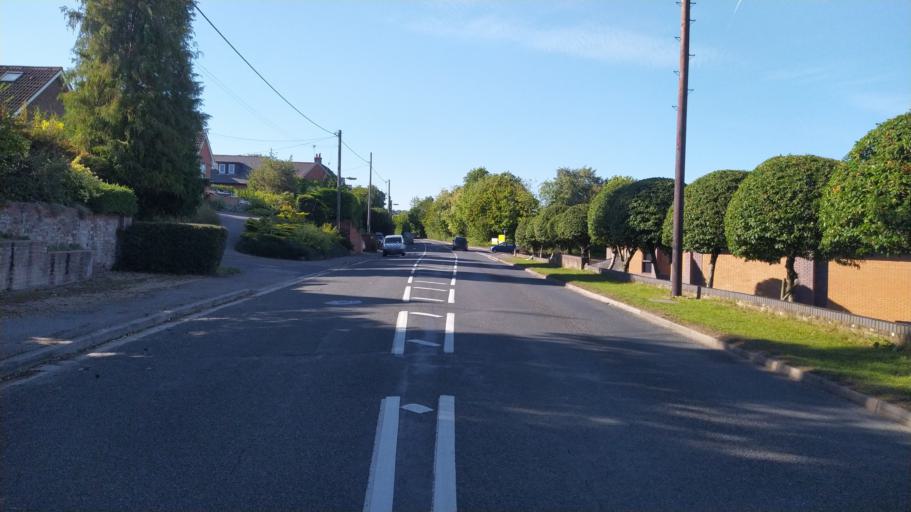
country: GB
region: England
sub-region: Hampshire
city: Alton
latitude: 51.1472
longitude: -0.9622
